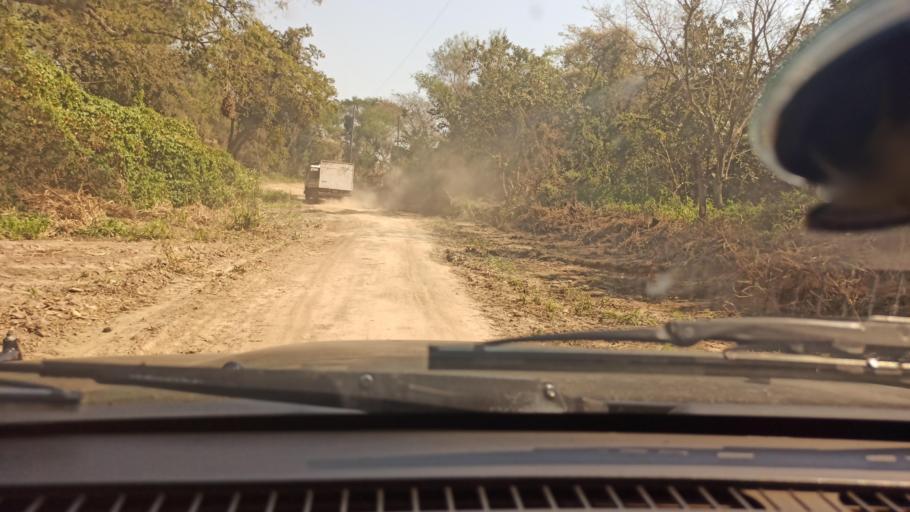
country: PY
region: Asuncion
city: Asuncion
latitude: -25.3386
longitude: -57.6797
